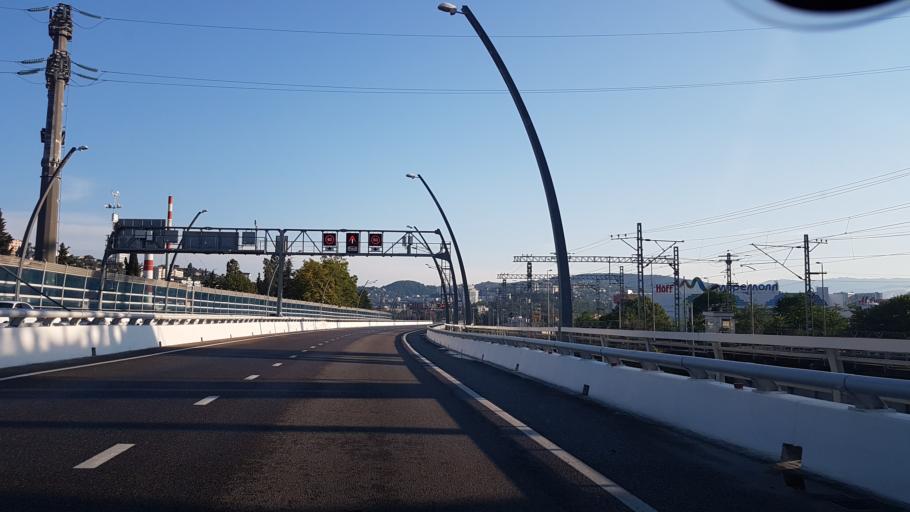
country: RU
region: Krasnodarskiy
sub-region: Sochi City
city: Sochi
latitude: 43.6006
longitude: 39.7300
